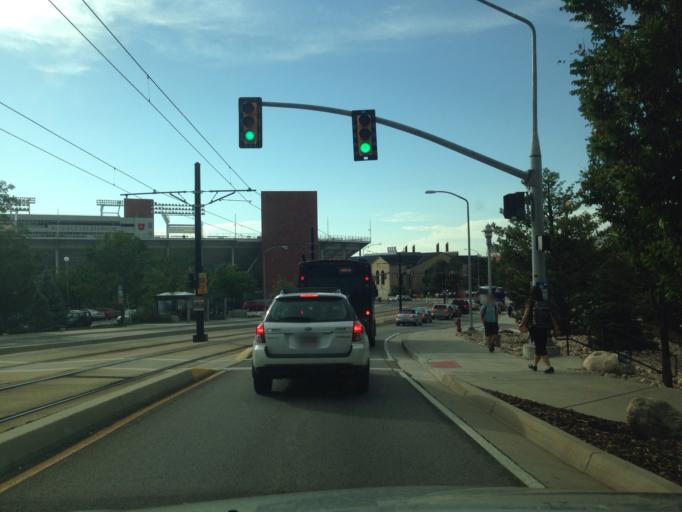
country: US
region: Utah
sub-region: Salt Lake County
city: Salt Lake City
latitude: 40.7601
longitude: -111.8460
